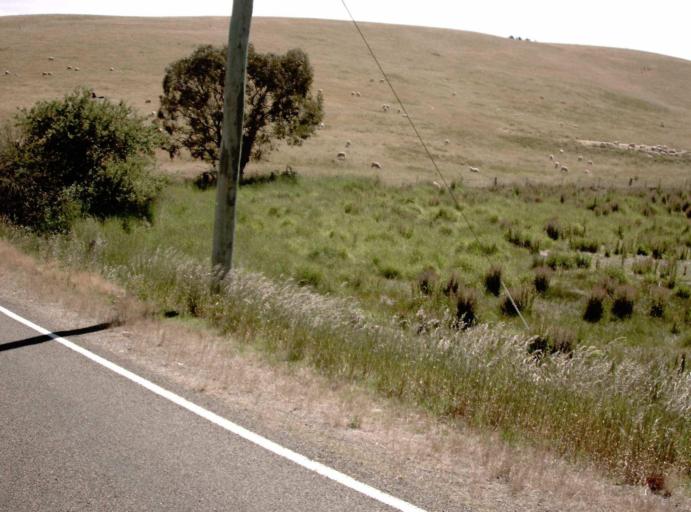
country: AU
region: Victoria
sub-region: Alpine
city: Mount Beauty
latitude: -37.0709
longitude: 147.6035
